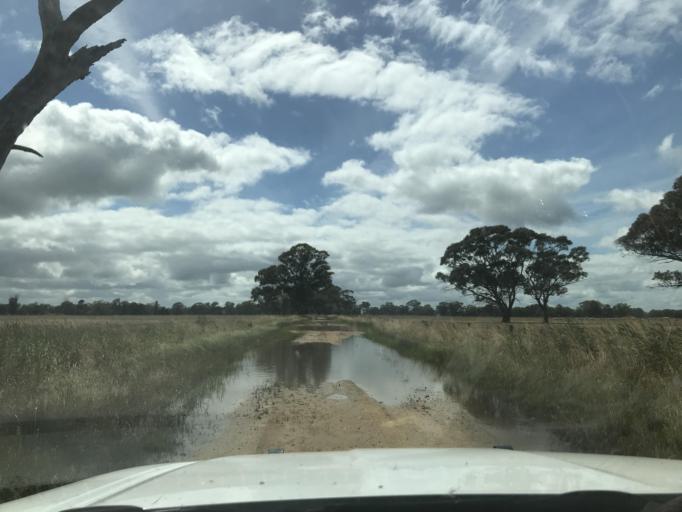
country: AU
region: South Australia
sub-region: Naracoorte and Lucindale
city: Naracoorte
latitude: -37.0097
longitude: 141.0755
